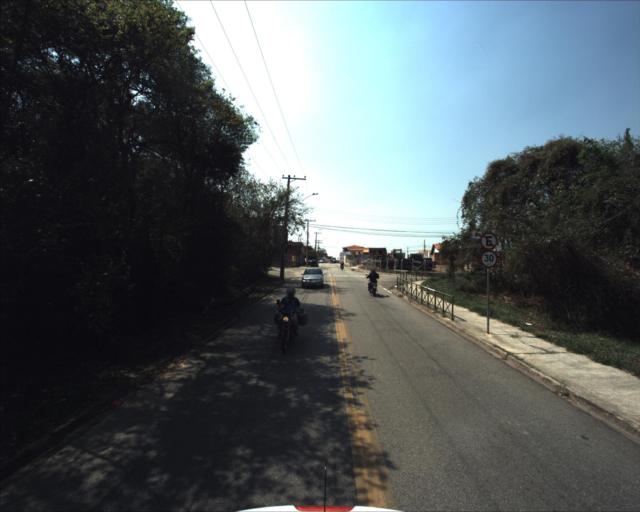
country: BR
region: Sao Paulo
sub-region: Sorocaba
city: Sorocaba
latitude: -23.4391
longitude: -47.4833
